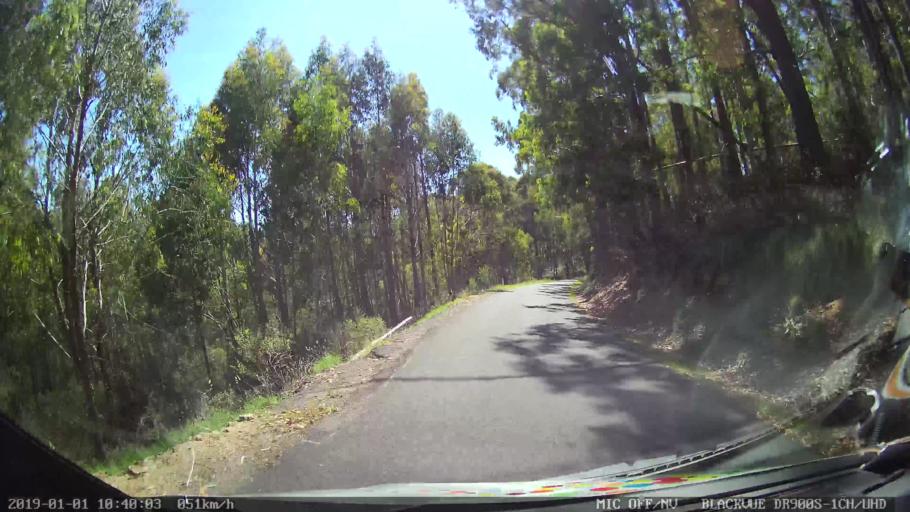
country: AU
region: New South Wales
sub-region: Snowy River
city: Jindabyne
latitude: -36.0389
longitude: 148.3098
